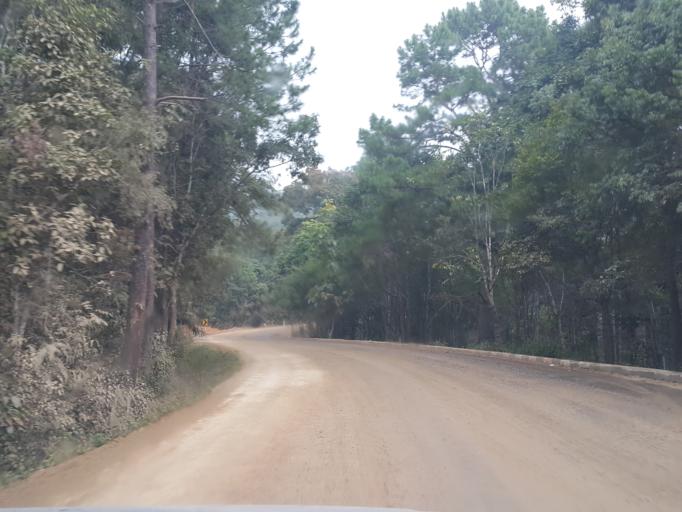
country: TH
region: Mae Hong Son
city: Mae Hi
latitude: 19.2698
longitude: 98.5797
